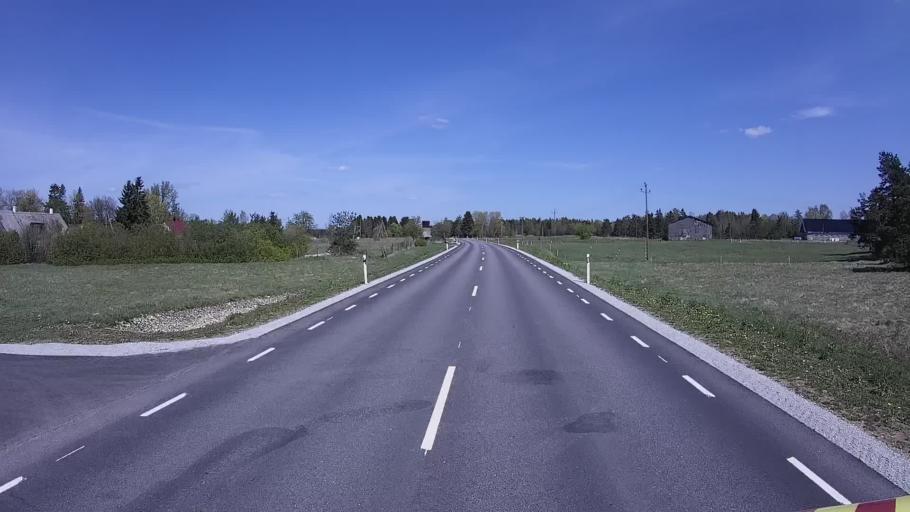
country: EE
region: Harju
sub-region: Nissi vald
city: Turba
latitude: 59.1807
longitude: 24.0841
